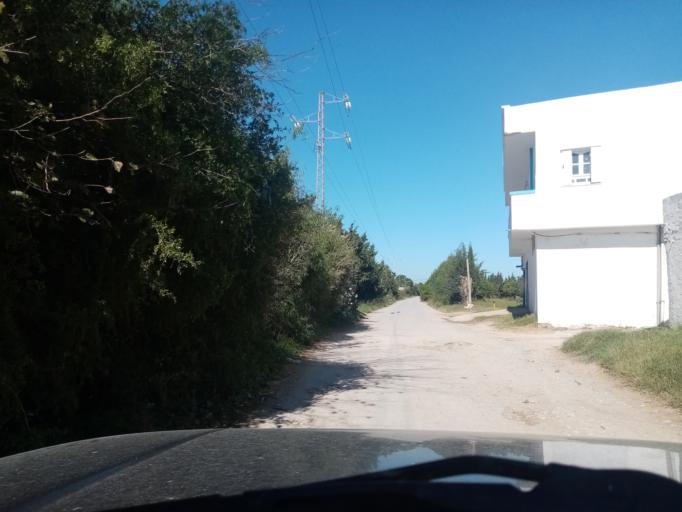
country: TN
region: Nabul
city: Bu `Urqub
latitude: 36.5701
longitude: 10.5767
